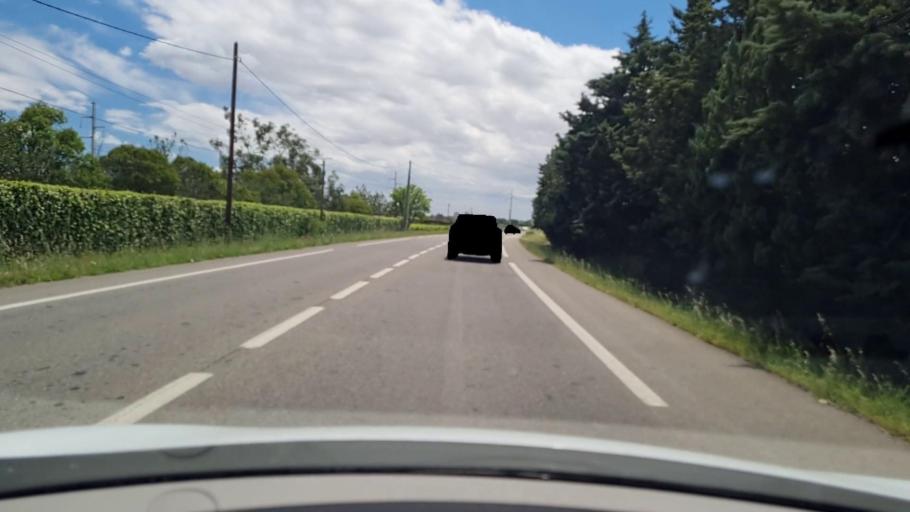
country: FR
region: Languedoc-Roussillon
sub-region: Departement du Gard
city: Le Cailar
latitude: 43.6915
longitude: 4.2519
